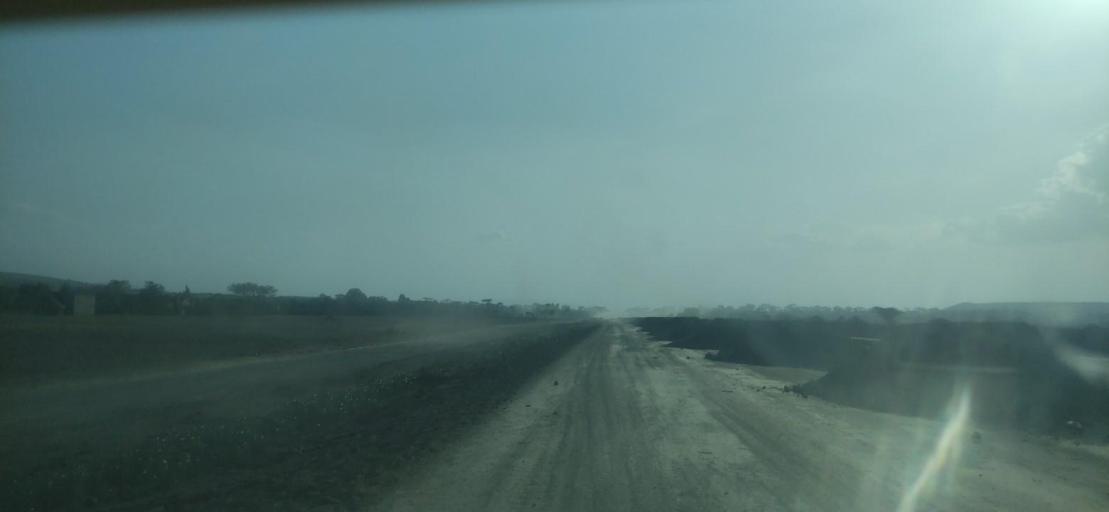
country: ET
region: Southern Nations, Nationalities, and People's Region
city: Hawassa
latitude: 7.1665
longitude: 38.4866
